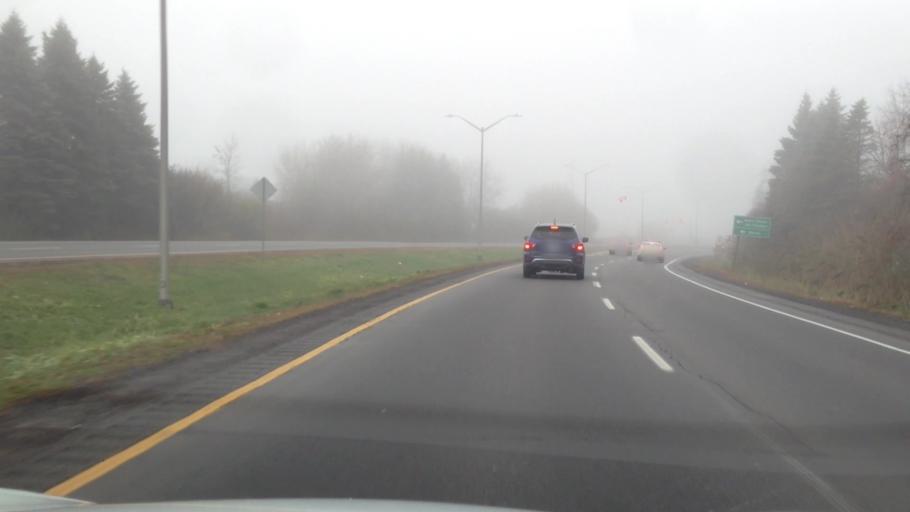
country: CA
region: Ontario
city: Ottawa
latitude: 45.4373
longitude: -75.5423
